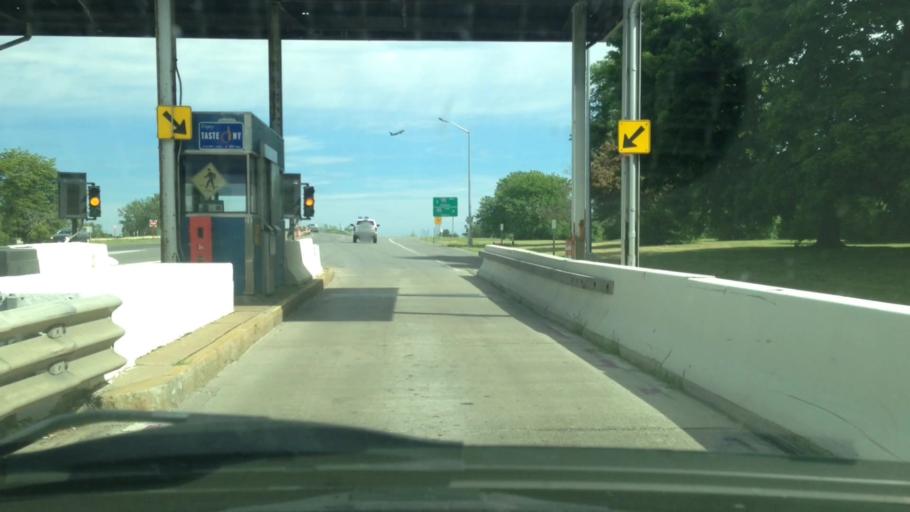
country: US
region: New York
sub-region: Onondaga County
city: East Syracuse
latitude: 43.0901
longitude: -76.0895
